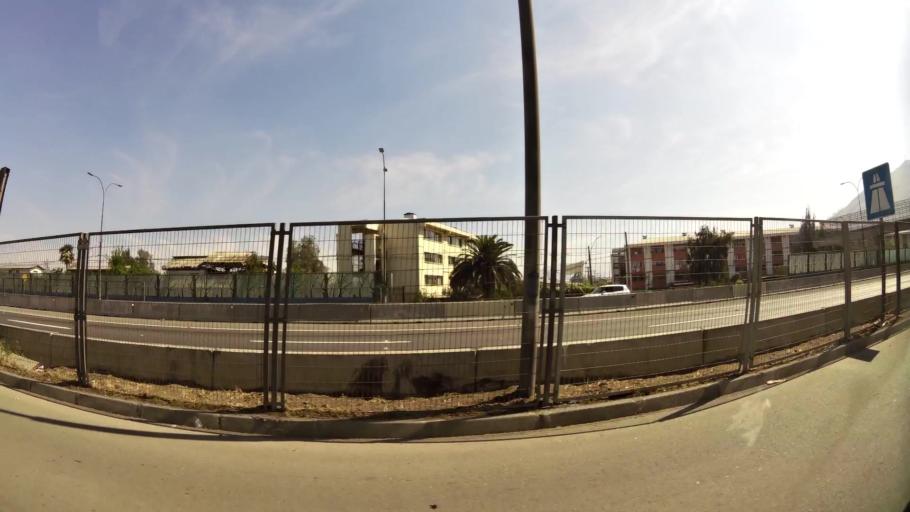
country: CL
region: Santiago Metropolitan
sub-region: Provincia de Santiago
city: Lo Prado
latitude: -33.4040
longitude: -70.6957
